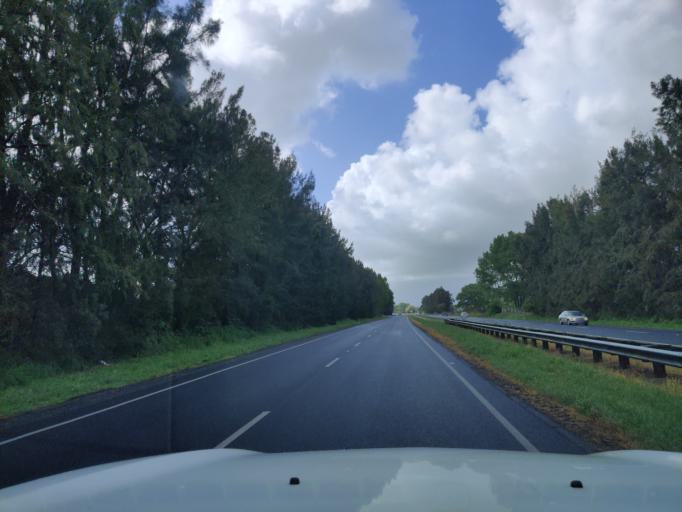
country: NZ
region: Waikato
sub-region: Waipa District
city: Cambridge
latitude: -37.8343
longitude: 175.3634
